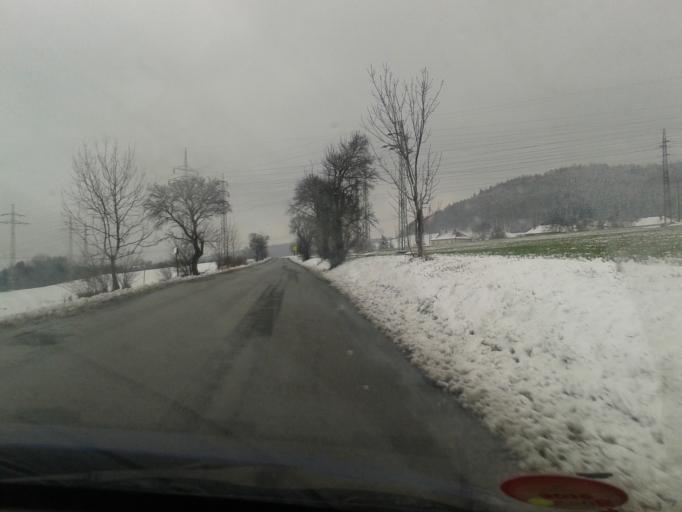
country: CZ
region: Central Bohemia
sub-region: Okres Beroun
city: Beroun
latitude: 49.9554
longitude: 14.0844
